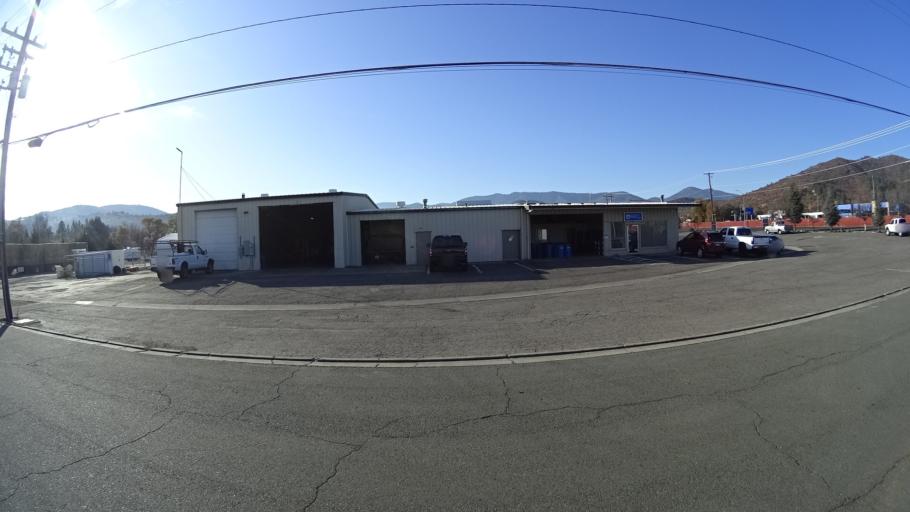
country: US
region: California
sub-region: Siskiyou County
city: Yreka
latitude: 41.7115
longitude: -122.6402
